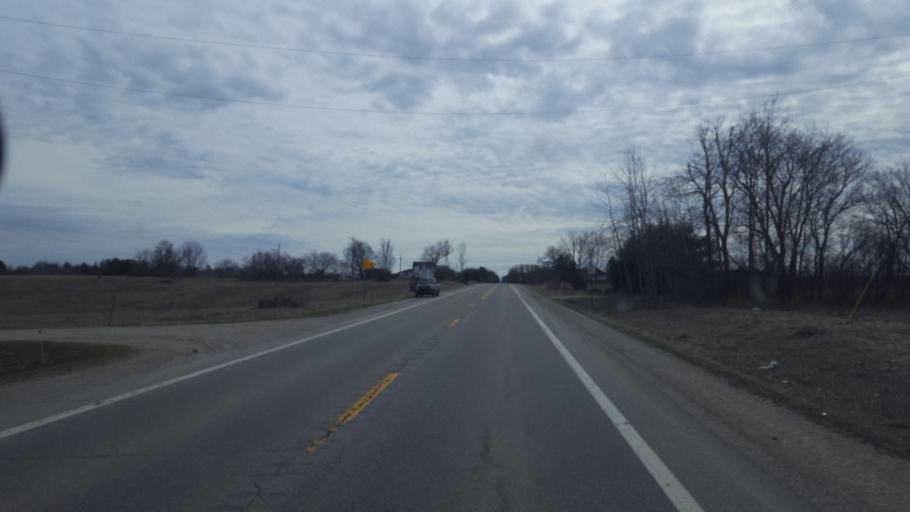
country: US
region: Michigan
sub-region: Isabella County
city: Lake Isabella
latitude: 43.7028
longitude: -85.1467
